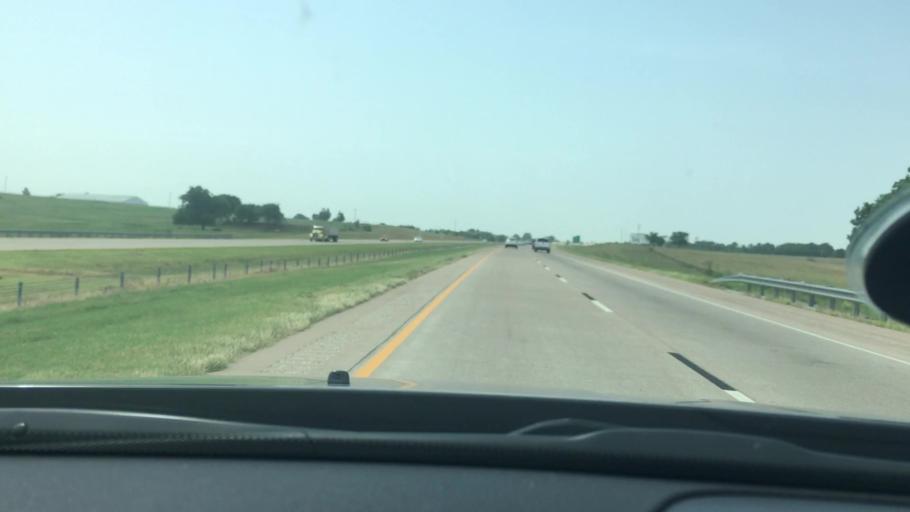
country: US
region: Oklahoma
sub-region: Garvin County
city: Wynnewood
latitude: 34.6632
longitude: -97.2225
